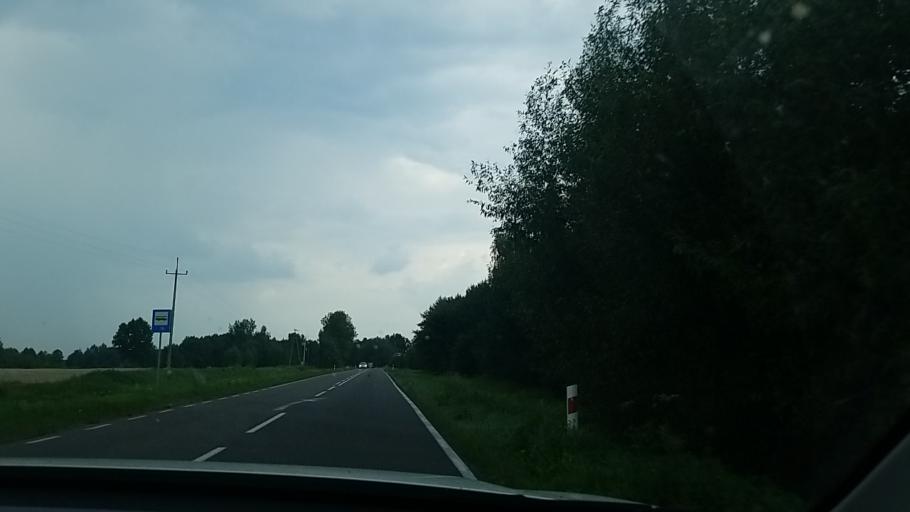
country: PL
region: Lublin Voivodeship
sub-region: Powiat leczynski
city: Cycow
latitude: 51.2405
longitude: 23.0883
